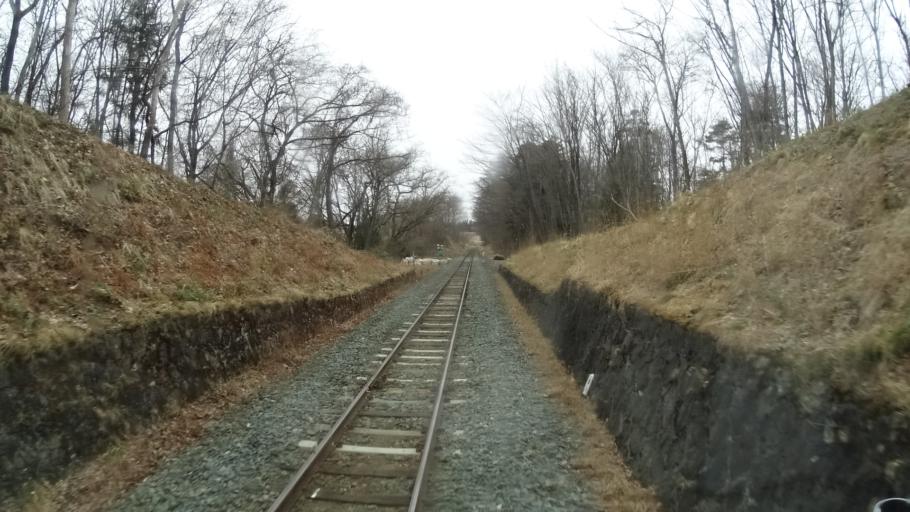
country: JP
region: Iwate
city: Hanamaki
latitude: 39.3917
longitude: 141.2176
